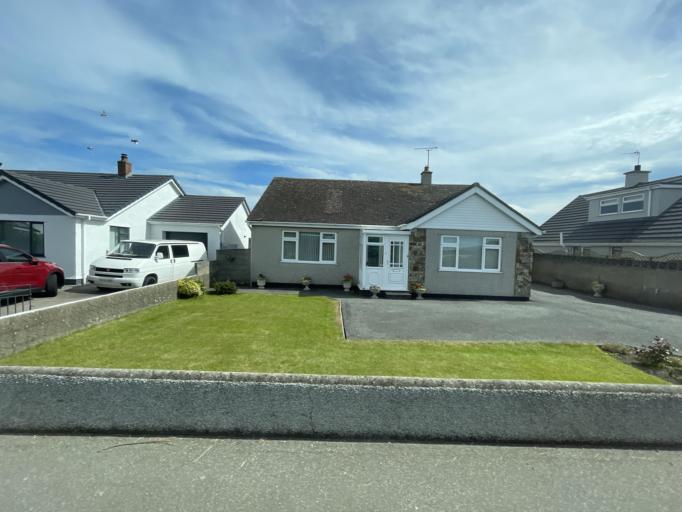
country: GB
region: Wales
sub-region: Anglesey
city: Valley
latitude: 53.2724
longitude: -4.5862
